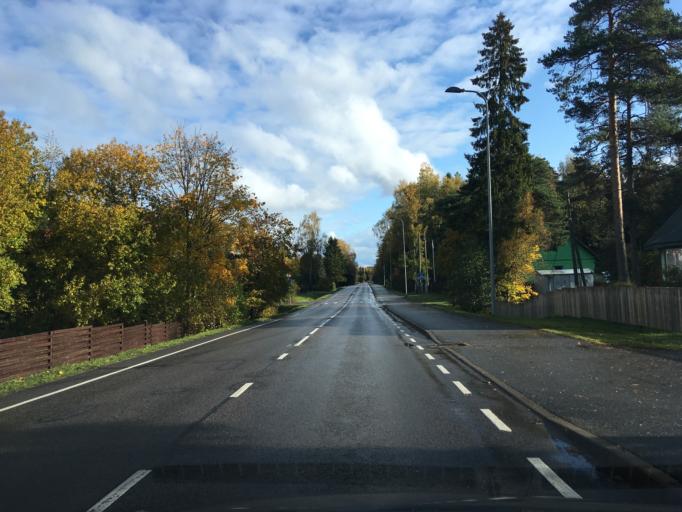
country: EE
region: Harju
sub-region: Raasiku vald
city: Raasiku
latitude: 59.1877
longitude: 25.1730
